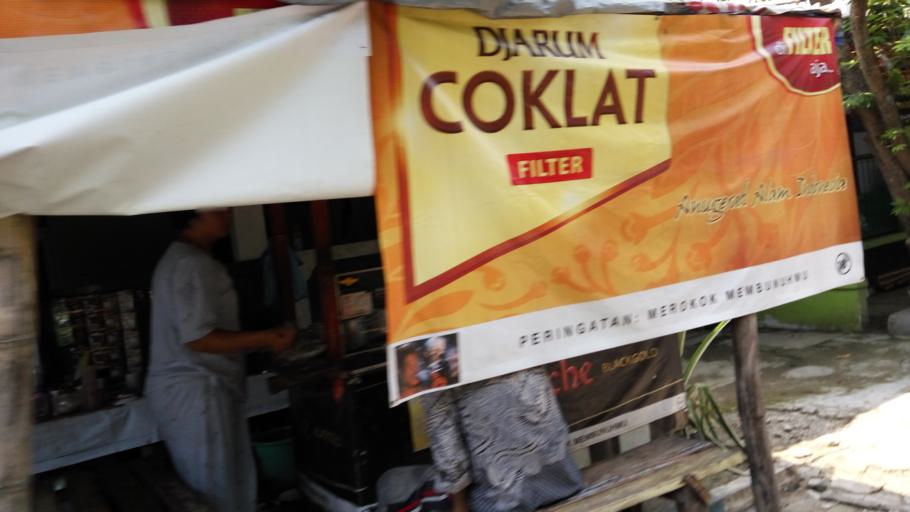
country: ID
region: Central Java
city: Mranggen
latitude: -7.0388
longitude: 110.4774
